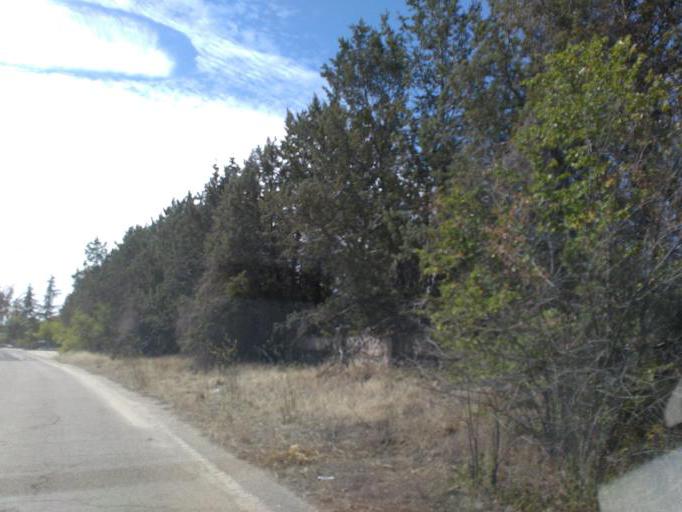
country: ES
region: Madrid
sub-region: Provincia de Madrid
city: Villanueva del Pardillo
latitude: 40.5211
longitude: -3.9415
